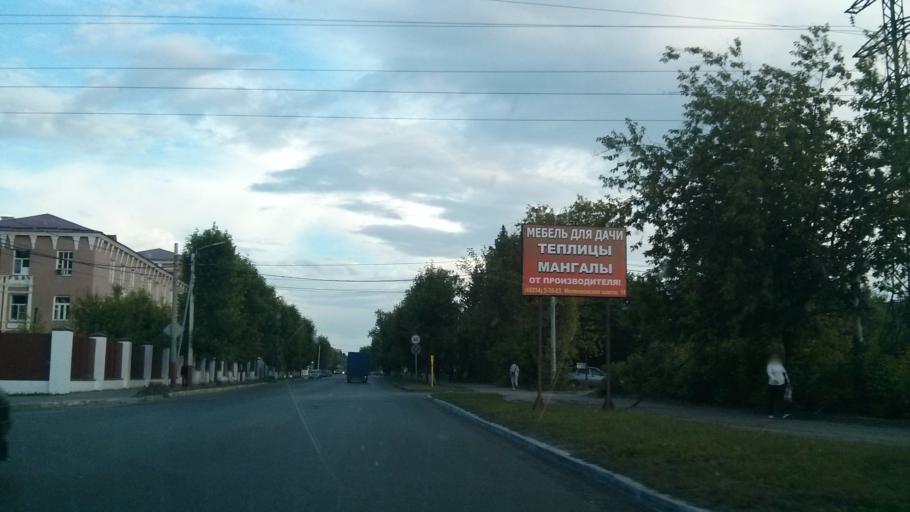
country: RU
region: Vladimir
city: Murom
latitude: 55.5584
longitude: 42.0594
